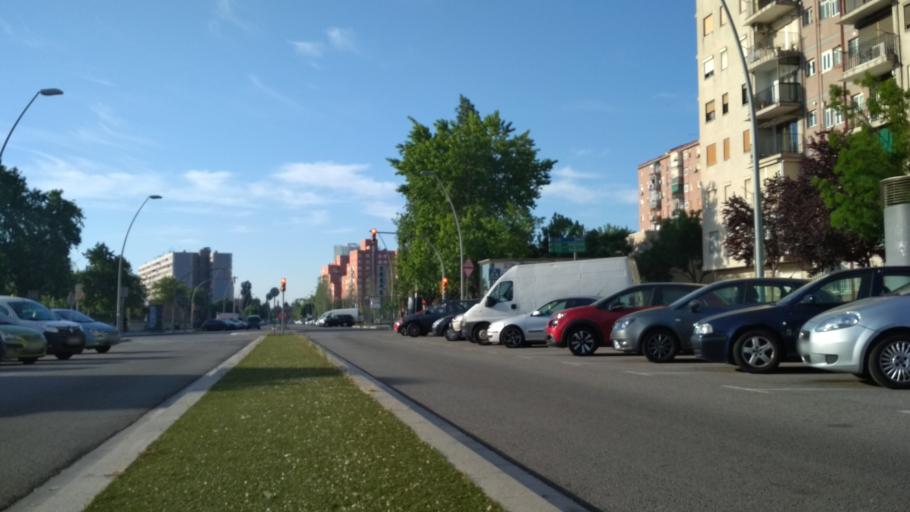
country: ES
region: Catalonia
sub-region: Provincia de Barcelona
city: Sant Adria de Besos
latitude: 41.4219
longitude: 2.2148
